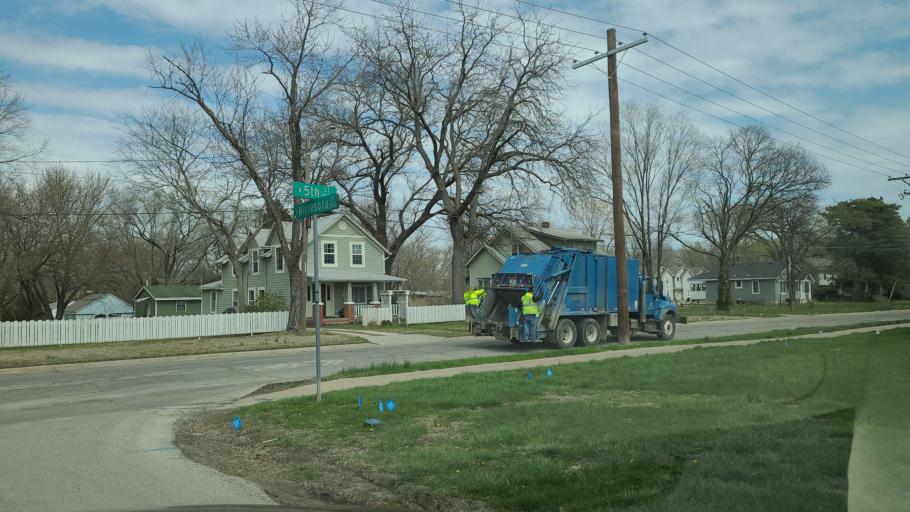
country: US
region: Kansas
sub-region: Douglas County
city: Lawrence
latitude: 38.9748
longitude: -95.2534
